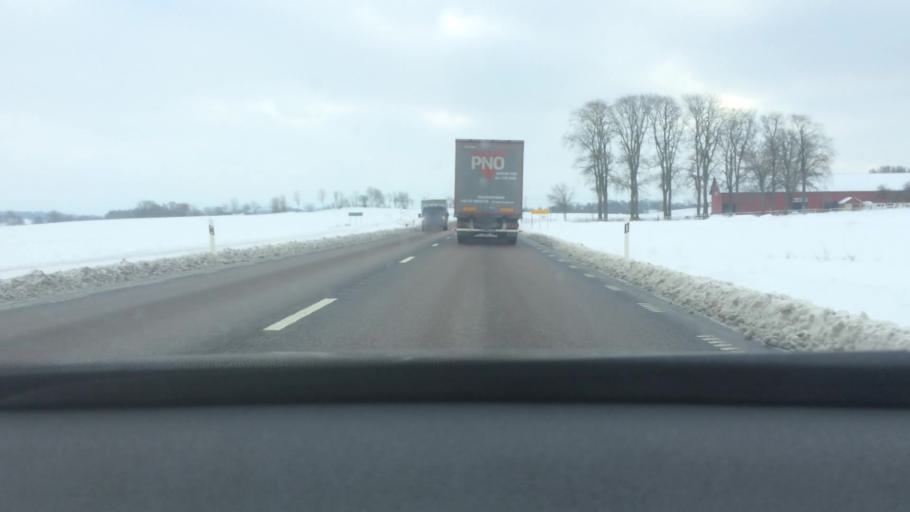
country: SE
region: Vaestra Goetaland
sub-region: Falkopings Kommun
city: Falkoeping
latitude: 58.2043
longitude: 13.5604
